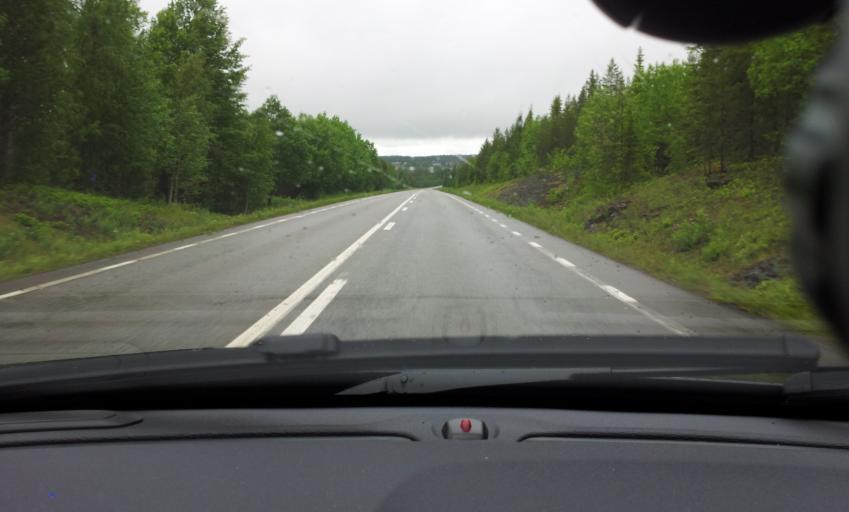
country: SE
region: Jaemtland
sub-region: Krokoms Kommun
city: Krokom
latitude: 63.5021
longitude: 14.5142
